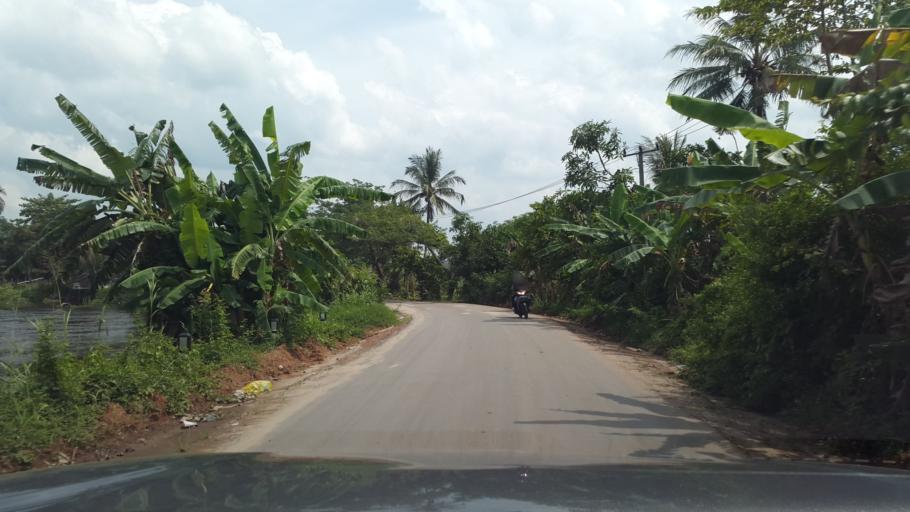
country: ID
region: South Sumatra
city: Tanjung Lubuk
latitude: -3.2678
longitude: 104.8700
